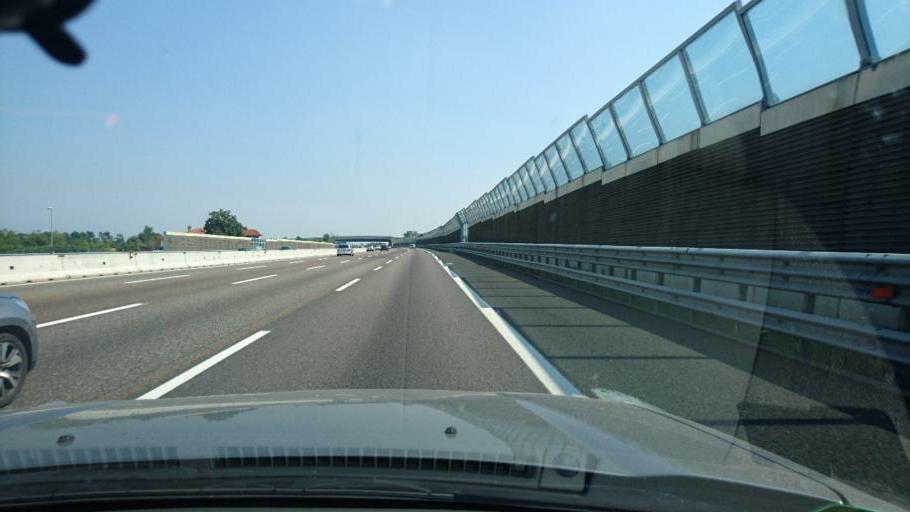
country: IT
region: Lombardy
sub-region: Provincia di Bergamo
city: Osio Sopra
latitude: 45.6220
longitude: 9.5796
